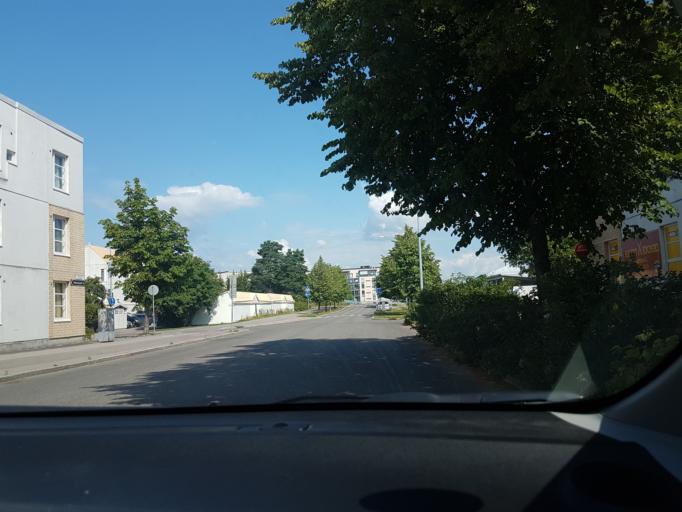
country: FI
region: Uusimaa
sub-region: Helsinki
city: Vantaa
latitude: 60.2030
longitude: 25.1275
